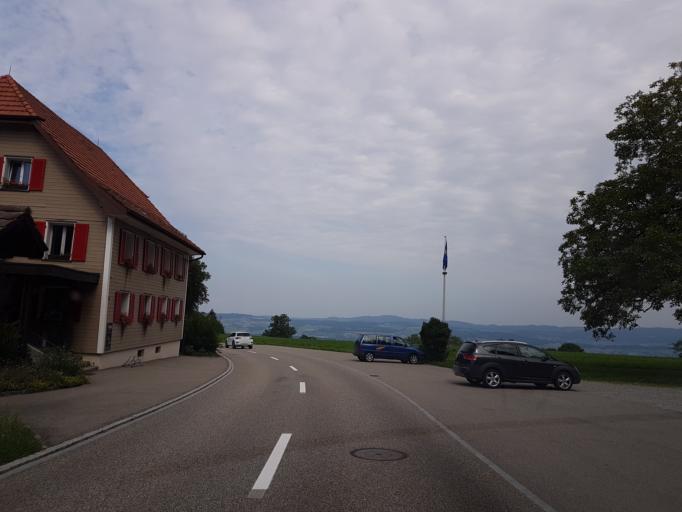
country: CH
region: Aargau
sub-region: Bezirk Muri
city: Buttwil
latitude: 47.2724
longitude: 8.2965
